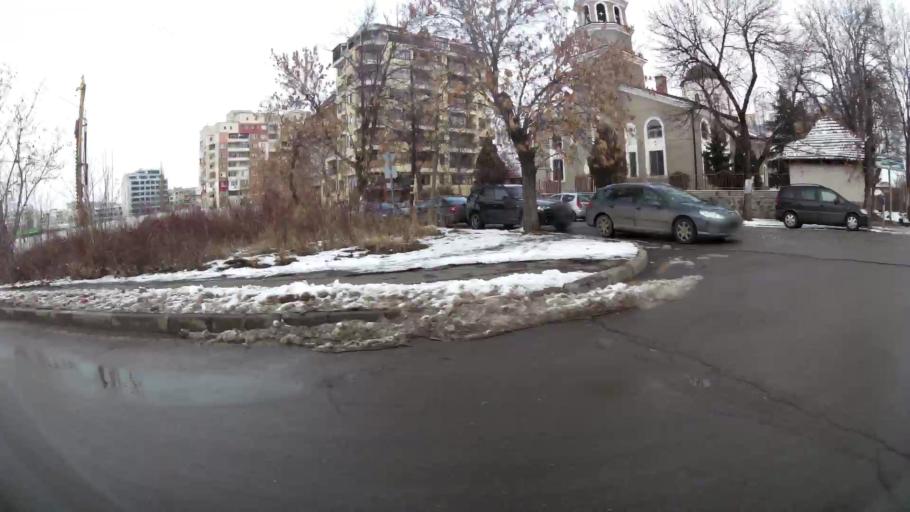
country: BG
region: Sofia-Capital
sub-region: Stolichna Obshtina
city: Sofia
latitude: 42.7005
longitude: 23.3520
